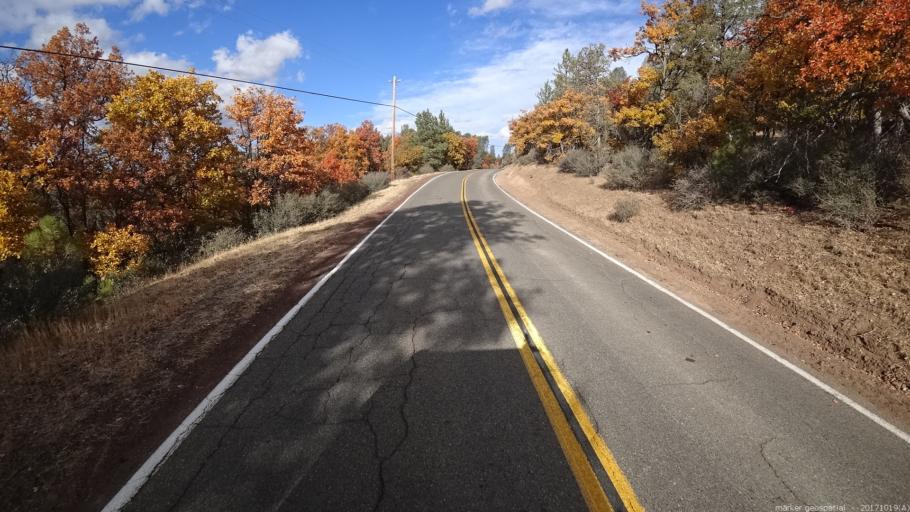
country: US
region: California
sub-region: Shasta County
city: Burney
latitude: 40.9862
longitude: -121.4326
